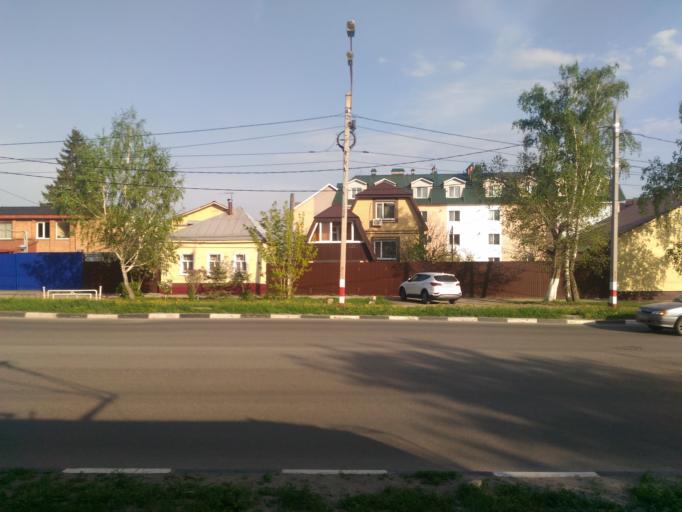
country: RU
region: Ulyanovsk
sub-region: Ulyanovskiy Rayon
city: Ulyanovsk
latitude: 54.3041
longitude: 48.3873
